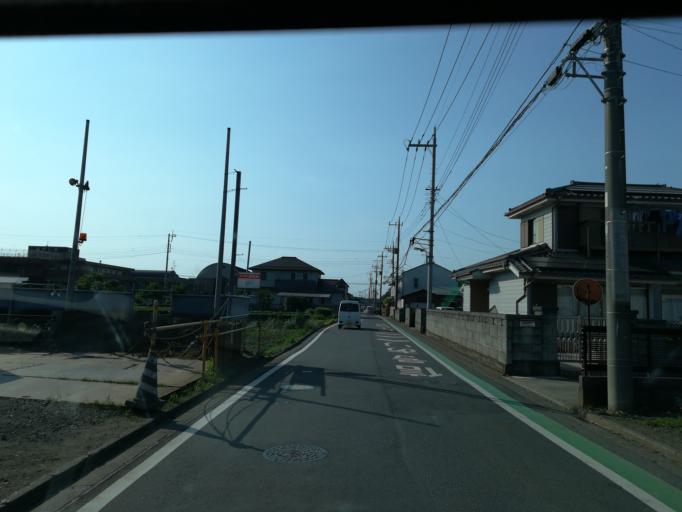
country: JP
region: Saitama
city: Sayama
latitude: 35.7965
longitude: 139.4060
